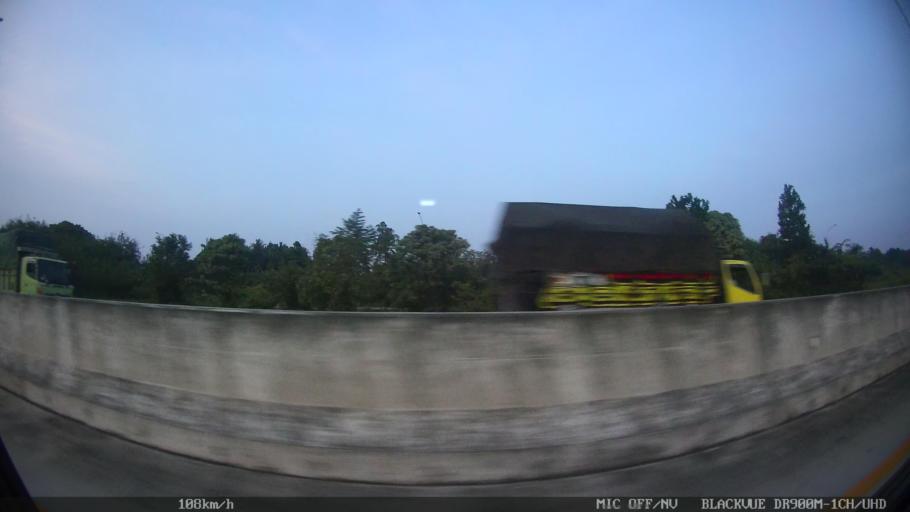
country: ID
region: Lampung
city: Kalianda
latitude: -5.6940
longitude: 105.6238
